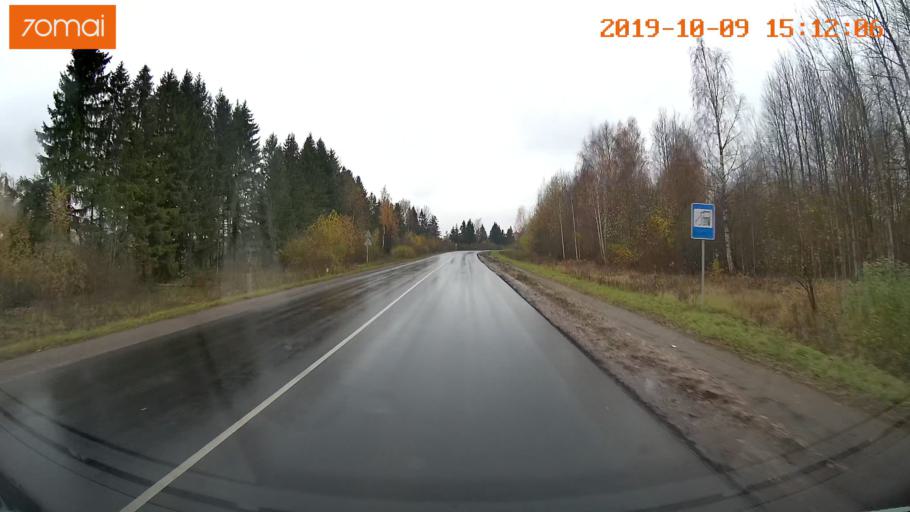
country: RU
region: Kostroma
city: Susanino
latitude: 58.1575
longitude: 41.6235
